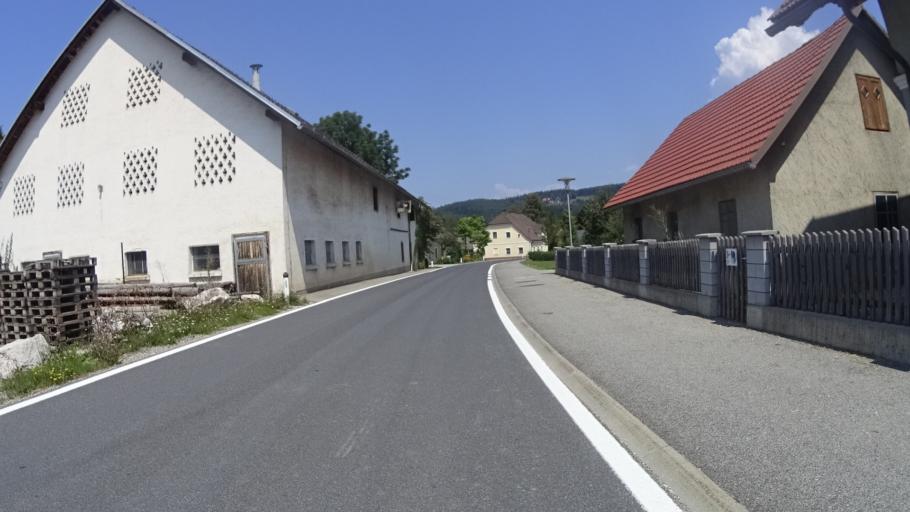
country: AT
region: Carinthia
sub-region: Politischer Bezirk Volkermarkt
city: Feistritz ob Bleiburg
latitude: 46.5733
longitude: 14.7707
